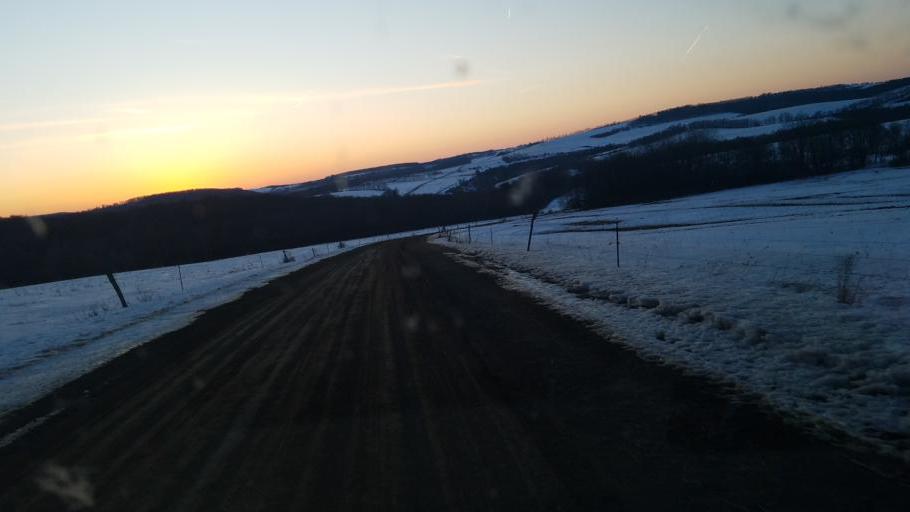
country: US
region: New York
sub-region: Allegany County
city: Andover
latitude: 42.0074
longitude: -77.7459
